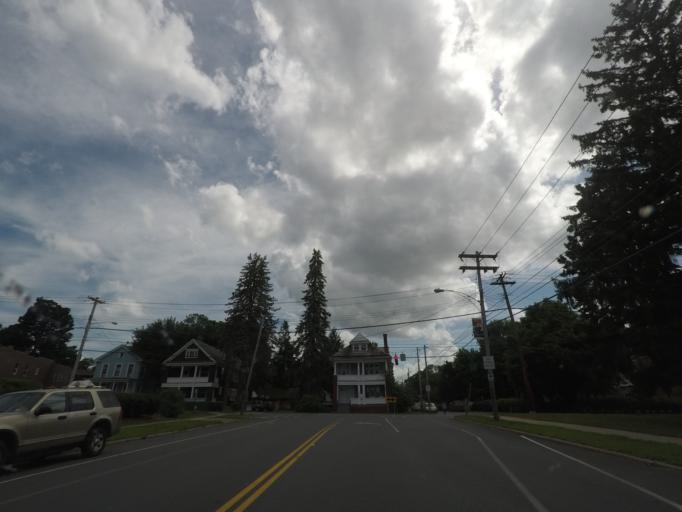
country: US
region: New York
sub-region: Rensselaer County
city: Troy
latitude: 42.7252
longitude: -73.6737
